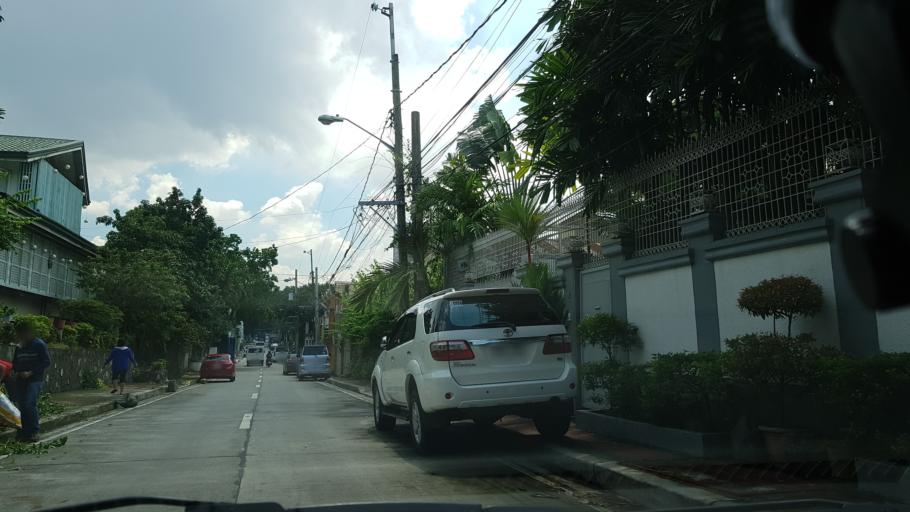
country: PH
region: Calabarzon
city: Del Monte
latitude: 14.6315
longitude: 121.0258
